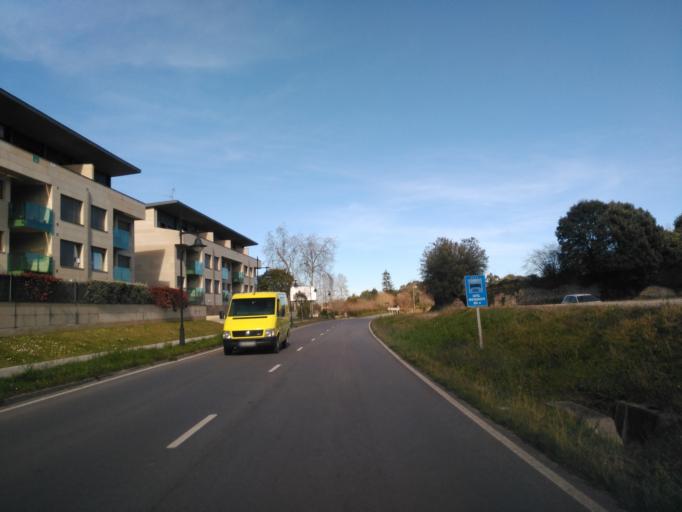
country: ES
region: Asturias
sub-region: Province of Asturias
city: Llanes
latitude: 43.4089
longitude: -4.7573
